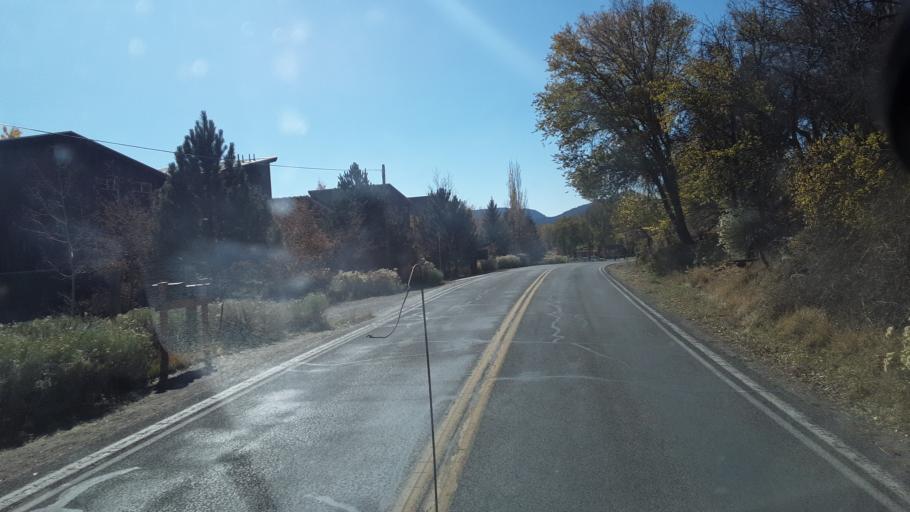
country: US
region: Colorado
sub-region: La Plata County
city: Durango
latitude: 37.3105
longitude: -107.8555
